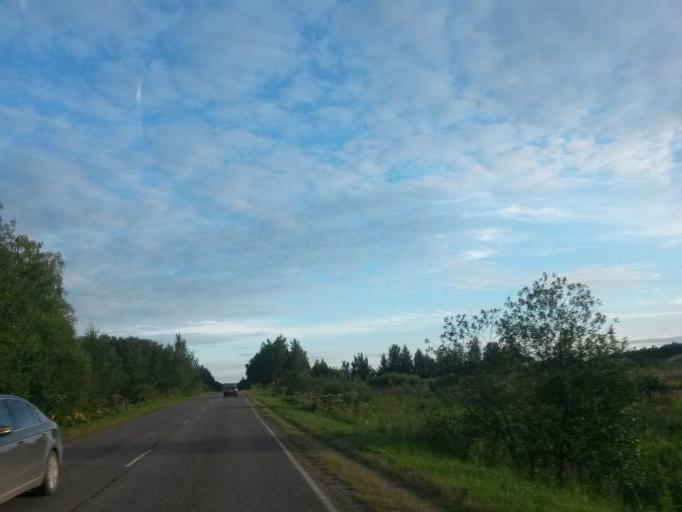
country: RU
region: Moskovskaya
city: Belyye Stolby
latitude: 55.2791
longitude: 37.7726
